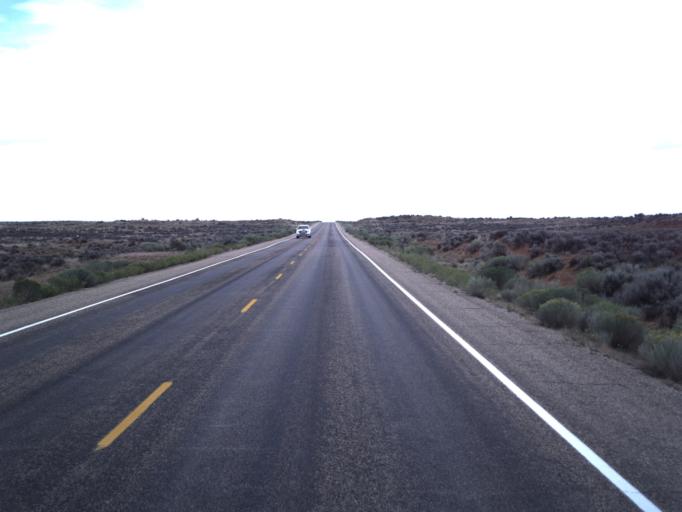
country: US
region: Utah
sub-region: Uintah County
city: Naples
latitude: 40.1606
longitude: -109.3099
